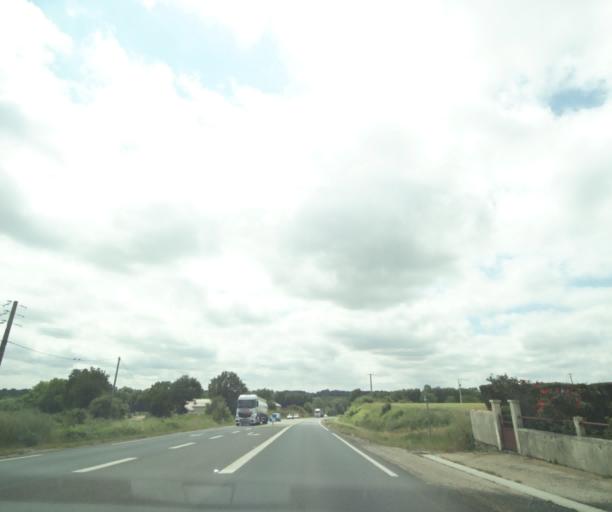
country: FR
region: Poitou-Charentes
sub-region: Departement des Deux-Sevres
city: Saint-Jean-de-Thouars
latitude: 46.9205
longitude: -0.1967
